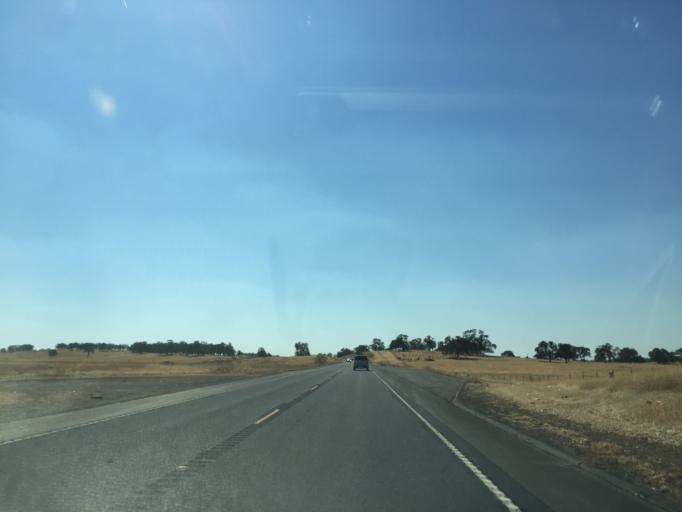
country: US
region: California
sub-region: Tuolumne County
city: Jamestown
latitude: 37.8622
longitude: -120.5119
